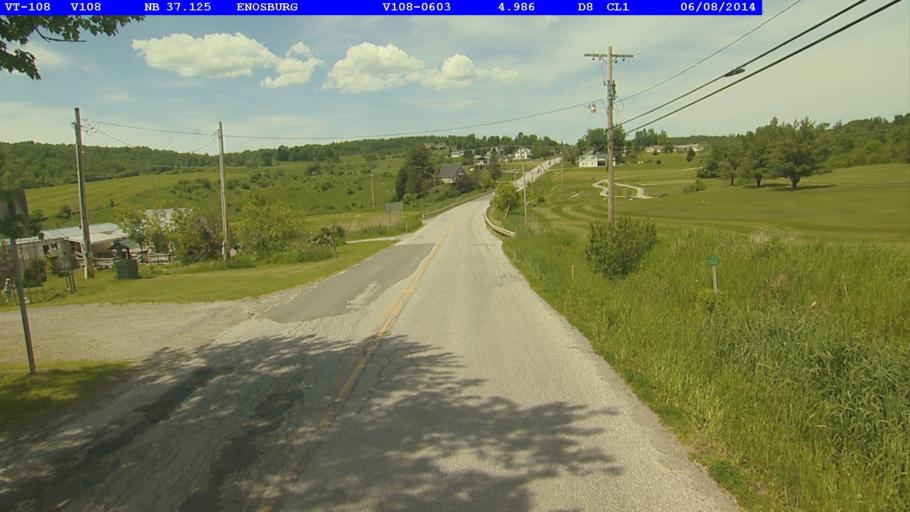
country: US
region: Vermont
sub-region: Franklin County
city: Enosburg Falls
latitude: 44.9124
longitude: -72.8038
